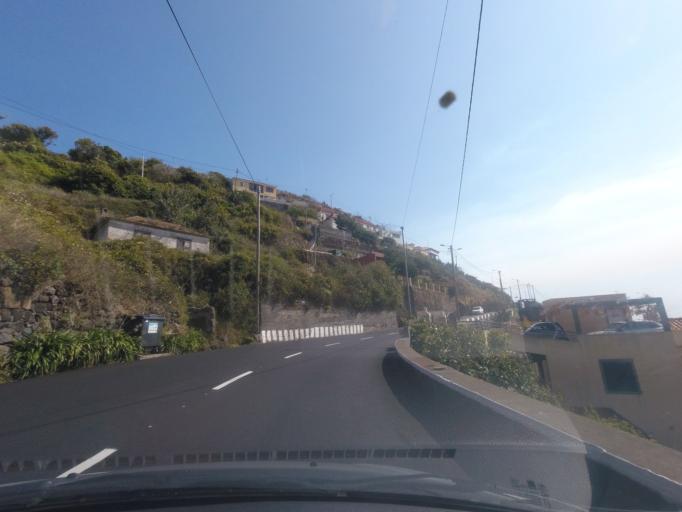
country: PT
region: Madeira
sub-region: Ribeira Brava
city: Campanario
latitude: 32.6685
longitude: -17.0374
